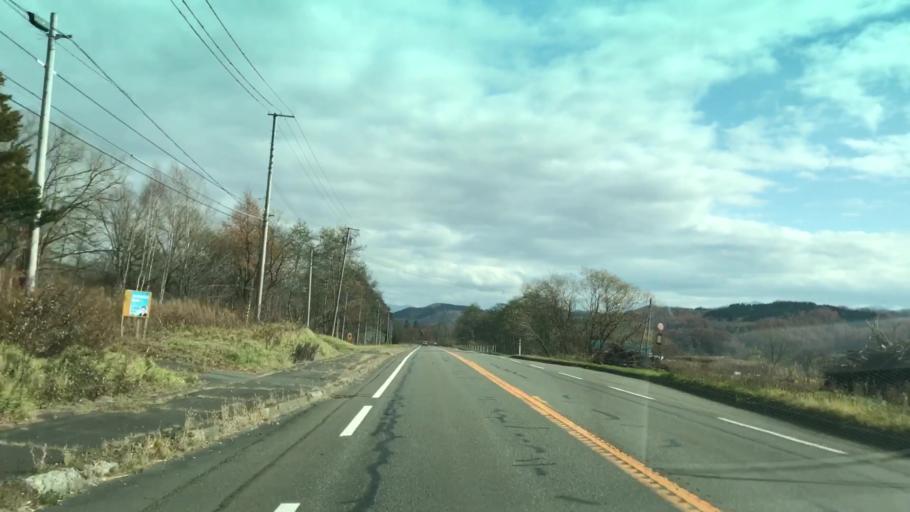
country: JP
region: Hokkaido
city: Shizunai-furukawacho
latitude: 42.7217
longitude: 142.2744
